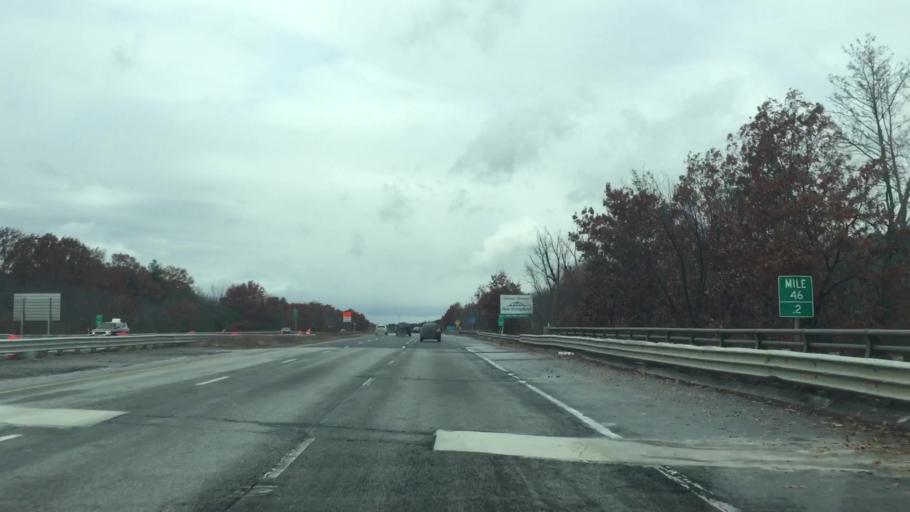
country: US
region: Massachusetts
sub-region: Essex County
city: Methuen
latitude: 42.7428
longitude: -71.2091
